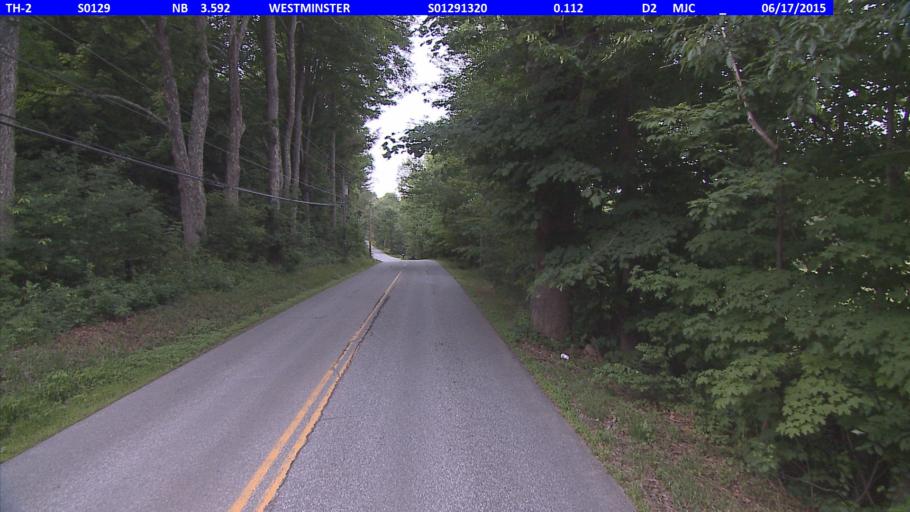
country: US
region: New Hampshire
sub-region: Cheshire County
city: Westmoreland
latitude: 43.0236
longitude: -72.5253
